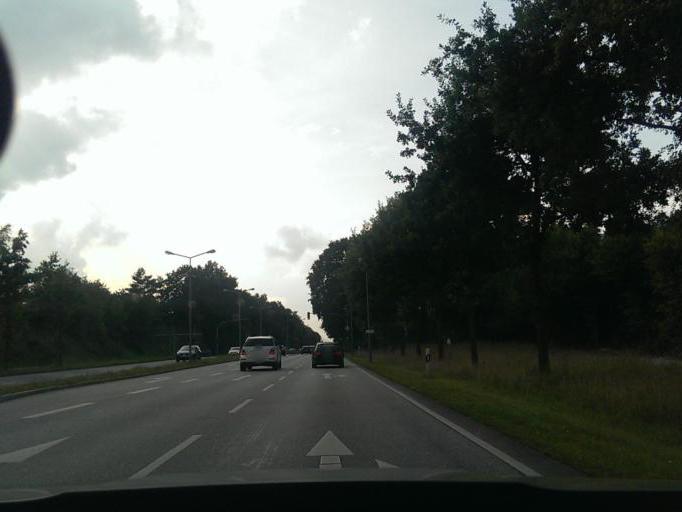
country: DE
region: Schleswig-Holstein
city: Norderstedt
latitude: 53.6473
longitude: 9.9600
